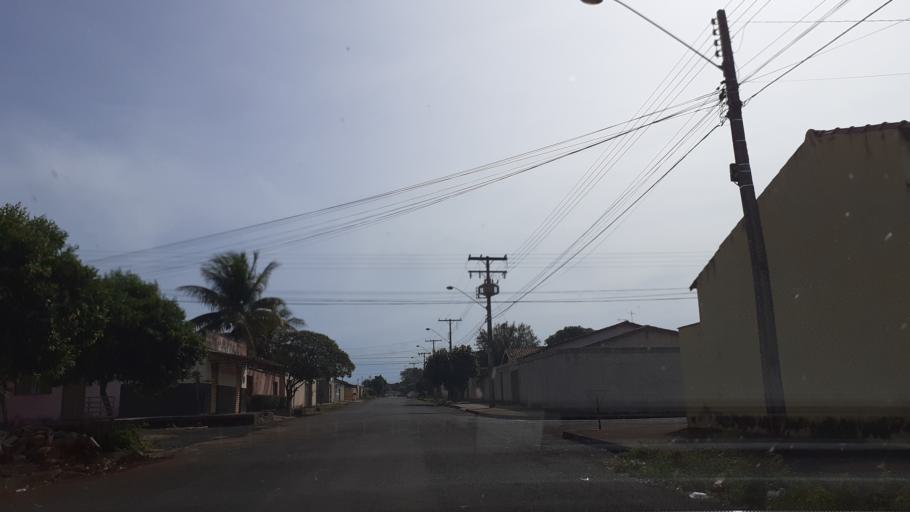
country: BR
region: Goias
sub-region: Itumbiara
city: Itumbiara
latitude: -18.4243
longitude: -49.2434
